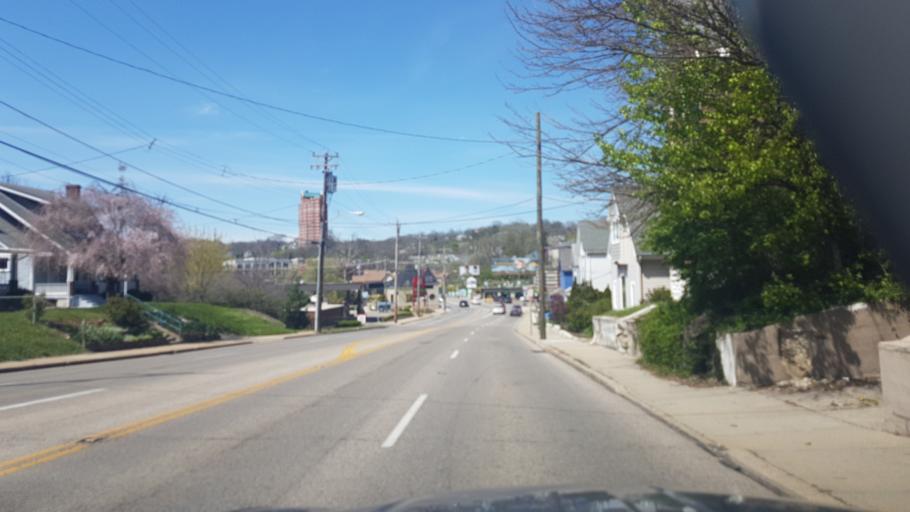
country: US
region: Kentucky
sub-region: Campbell County
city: Dayton
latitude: 39.1137
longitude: -84.4354
